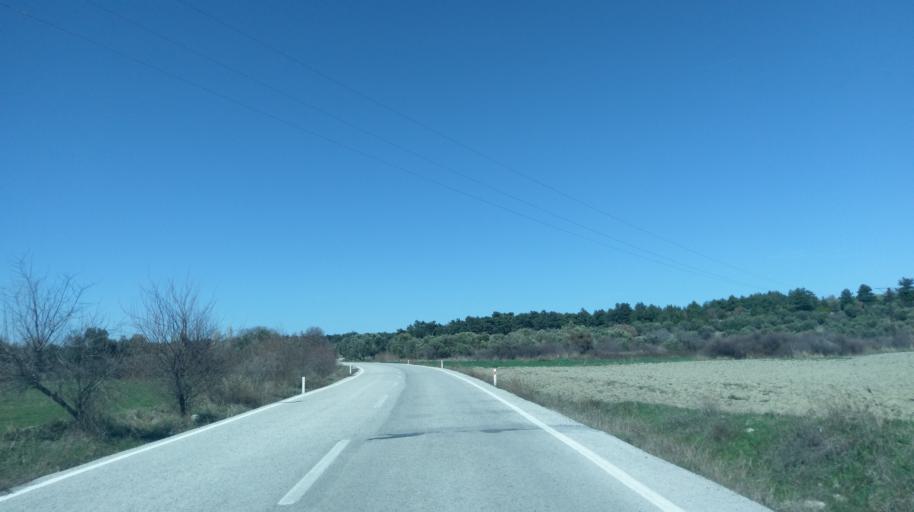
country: TR
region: Canakkale
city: Intepe
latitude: 40.0550
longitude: 26.2047
